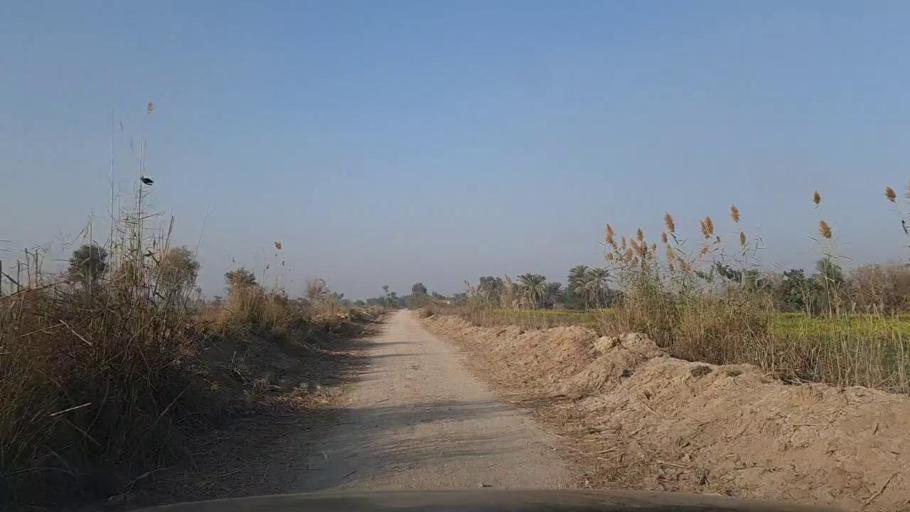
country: PK
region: Sindh
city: Daur
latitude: 26.4606
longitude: 68.4380
